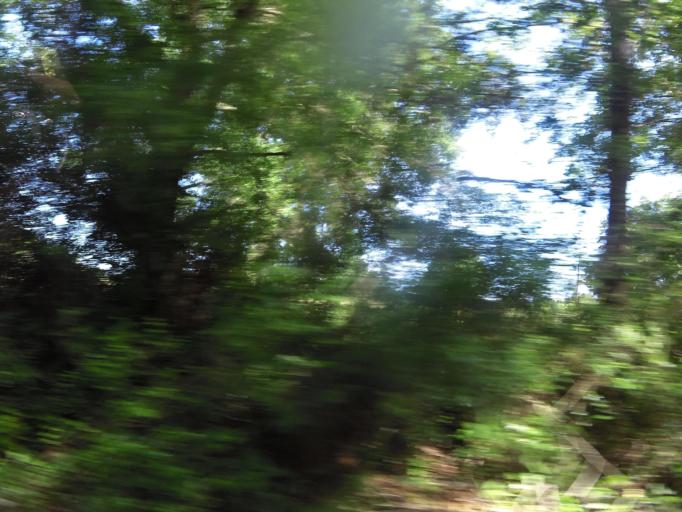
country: US
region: Florida
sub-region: Nassau County
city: Callahan
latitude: 30.5755
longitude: -81.7741
